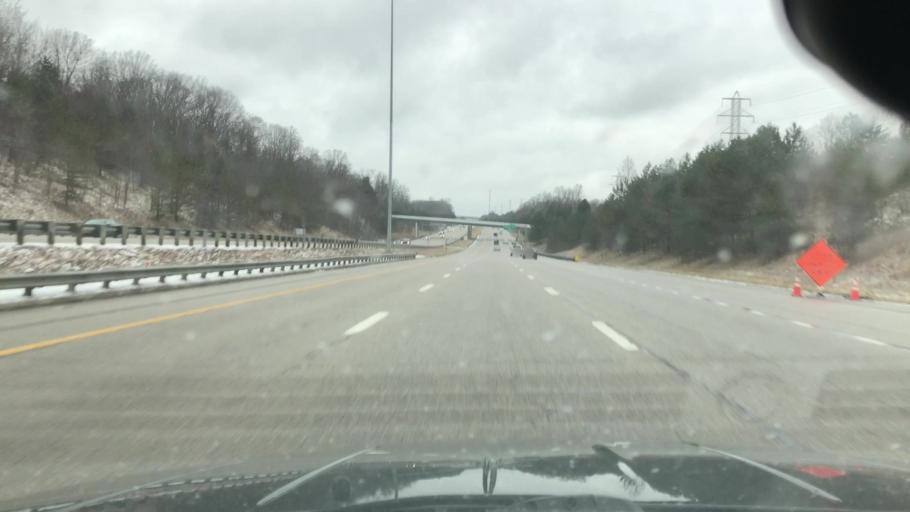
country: US
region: Ohio
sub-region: Cuyahoga County
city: Brecksville
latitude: 41.3217
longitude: -81.6486
